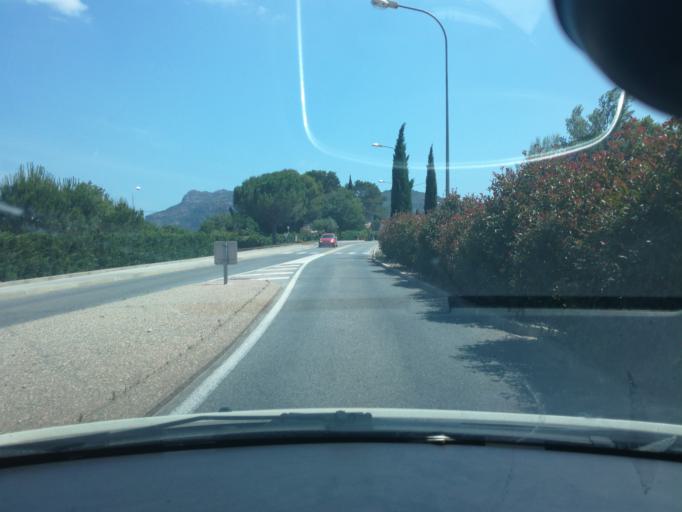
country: FR
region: Provence-Alpes-Cote d'Azur
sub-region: Departement du Var
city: Le Muy
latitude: 43.4792
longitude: 6.5659
